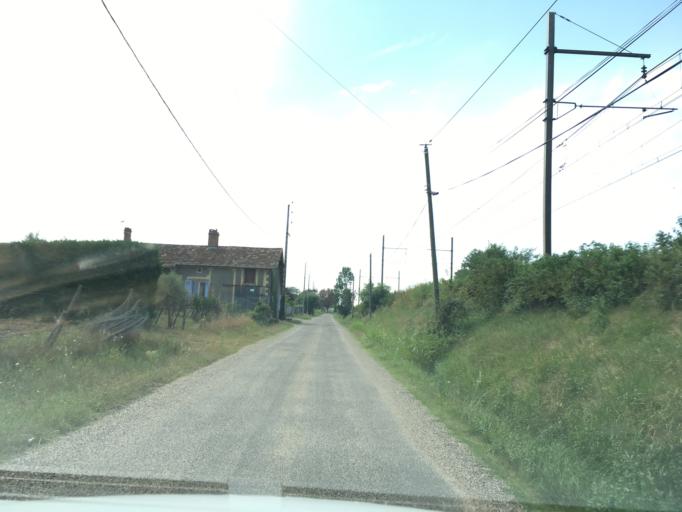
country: FR
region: Midi-Pyrenees
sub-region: Departement du Tarn-et-Garonne
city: Montbeton
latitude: 44.0160
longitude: 1.3193
